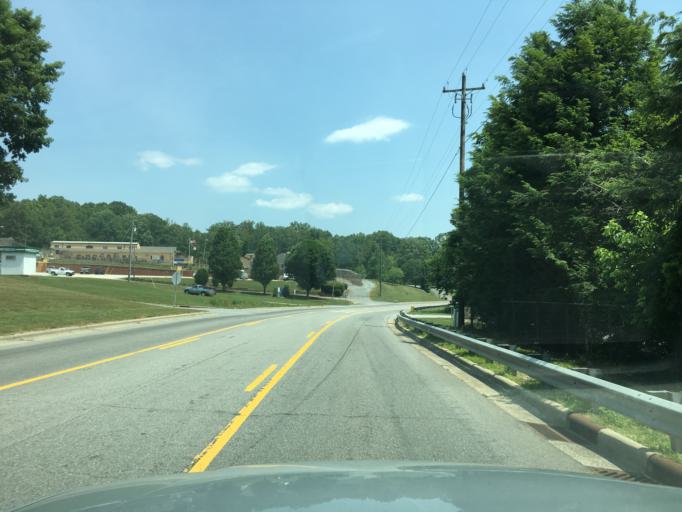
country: US
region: North Carolina
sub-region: McDowell County
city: Marion
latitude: 35.6526
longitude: -81.9560
